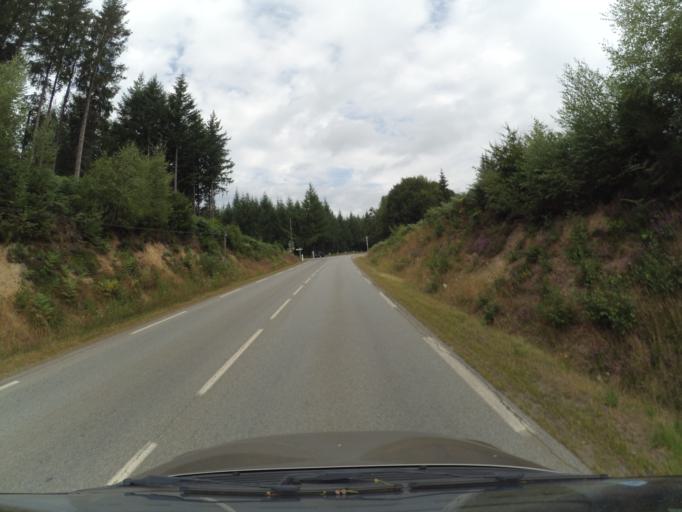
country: FR
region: Limousin
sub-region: Departement de la Correze
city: Ussel
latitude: 45.5914
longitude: 2.2907
